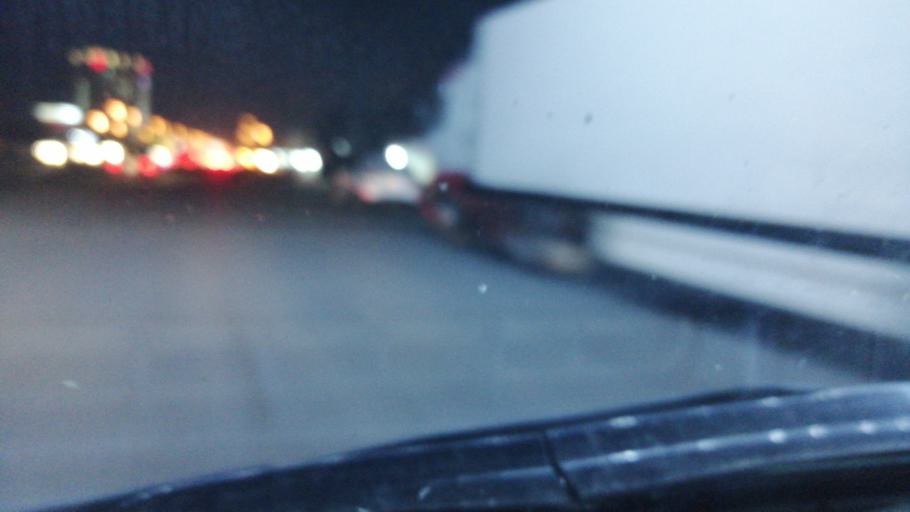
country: IQ
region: Arbil
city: Erbil
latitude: 36.1572
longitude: 43.9869
